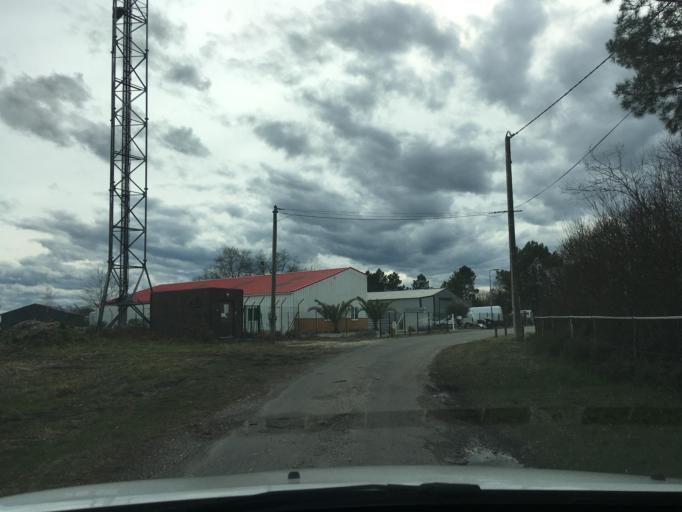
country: FR
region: Aquitaine
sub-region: Departement de la Gironde
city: Saint-Sauveur
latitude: 45.2216
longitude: -0.8715
